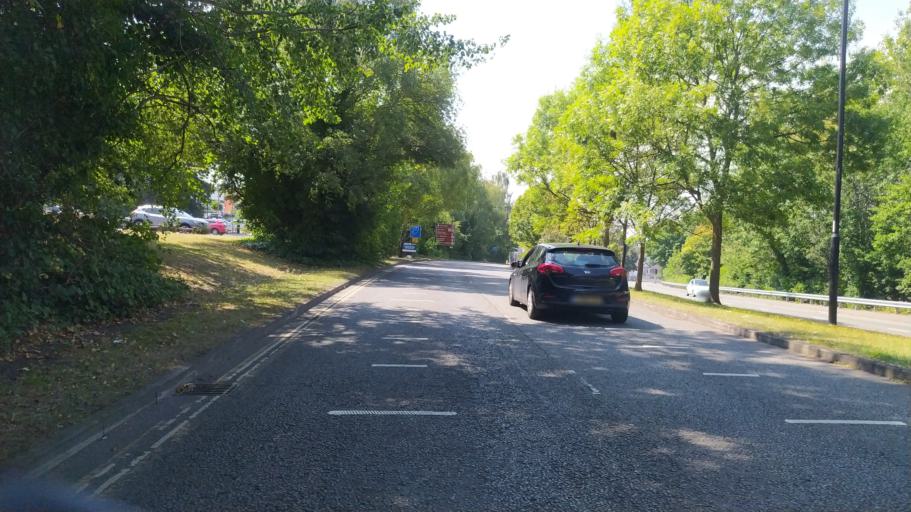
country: GB
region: England
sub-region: Hampshire
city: West End
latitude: 50.9155
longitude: -1.3619
